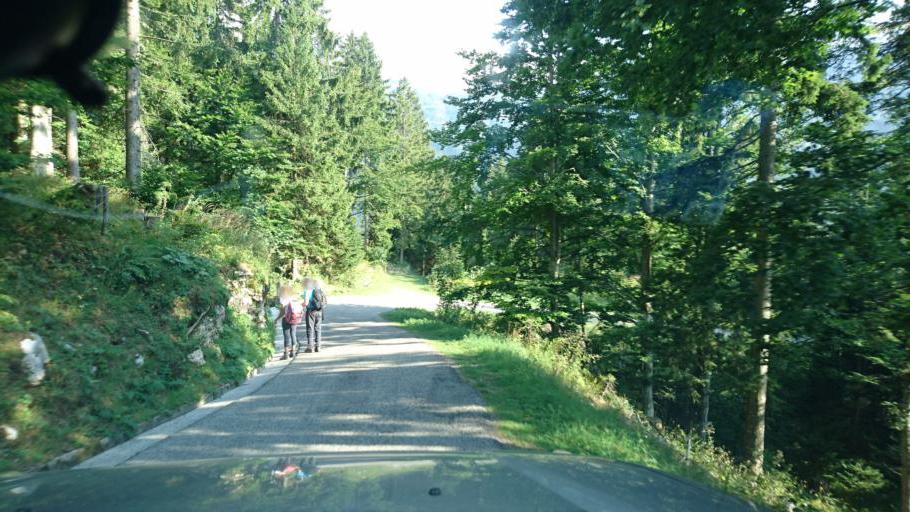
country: SI
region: Bovec
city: Bovec
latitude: 46.3938
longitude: 13.4674
